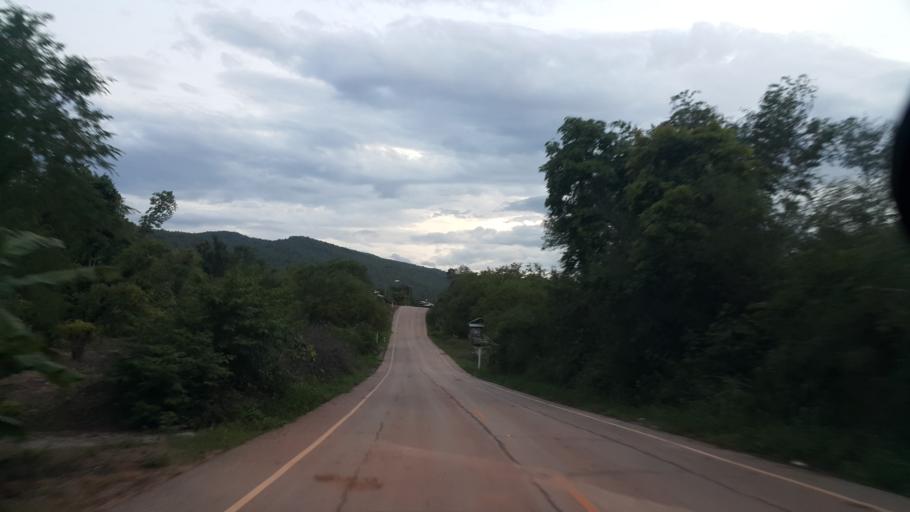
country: TH
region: Loei
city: Phu Ruea
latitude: 17.5115
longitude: 101.2328
